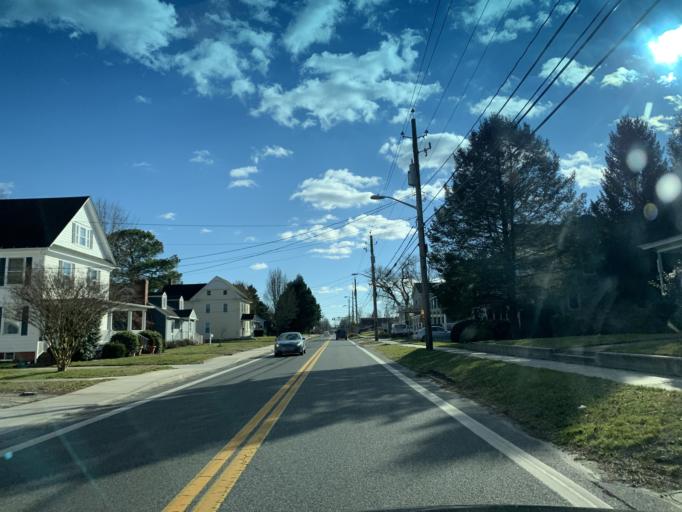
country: US
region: Maryland
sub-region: Worcester County
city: Berlin
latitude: 38.3323
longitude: -75.2208
